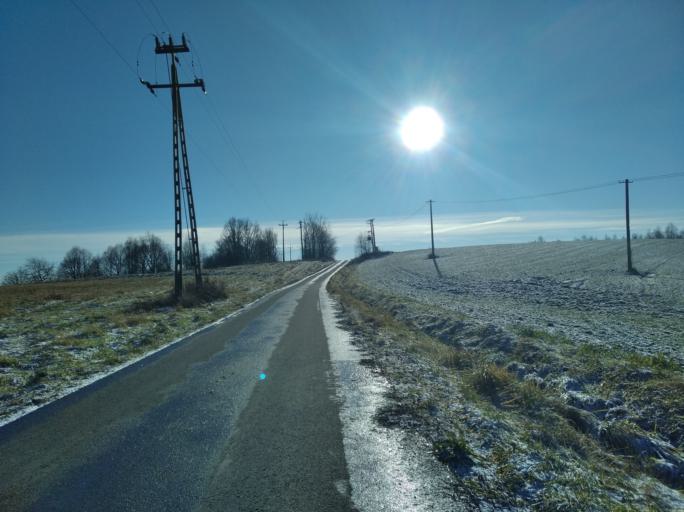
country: PL
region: Subcarpathian Voivodeship
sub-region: Powiat strzyzowski
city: Czudec
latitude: 49.9439
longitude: 21.7668
